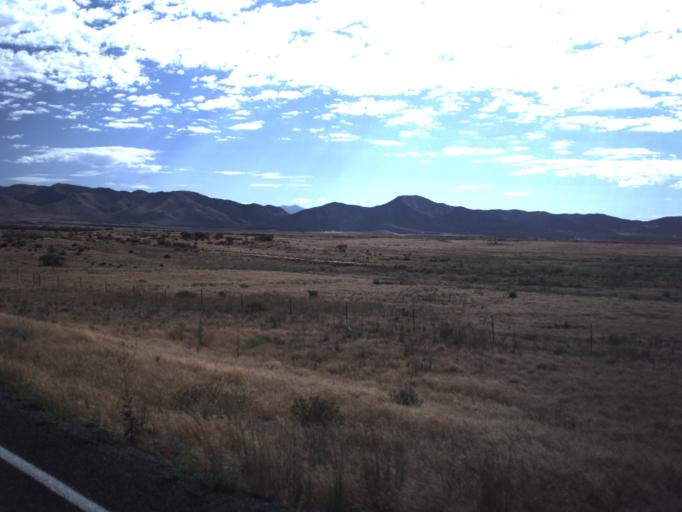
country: US
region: Utah
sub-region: Juab County
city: Mona
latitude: 39.7102
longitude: -112.2063
